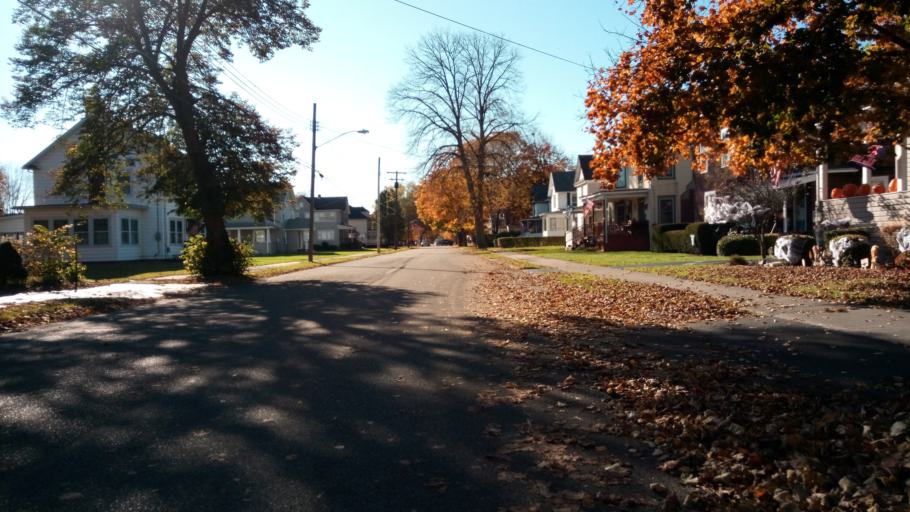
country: US
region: New York
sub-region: Chemung County
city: Southport
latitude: 42.0668
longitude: -76.8078
